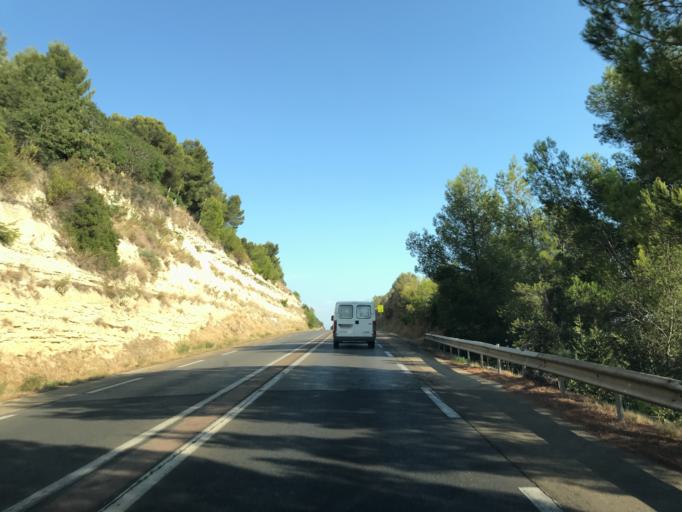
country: FR
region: Provence-Alpes-Cote d'Azur
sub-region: Departement des Bouches-du-Rhone
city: Saint-Chamas
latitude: 43.5530
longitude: 5.0355
